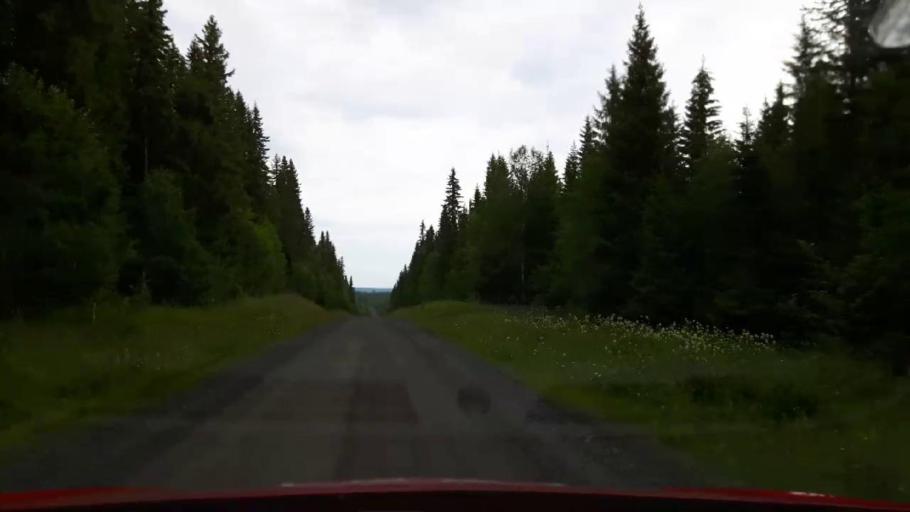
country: SE
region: Jaemtland
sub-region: OEstersunds Kommun
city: Lit
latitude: 63.3897
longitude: 15.2100
